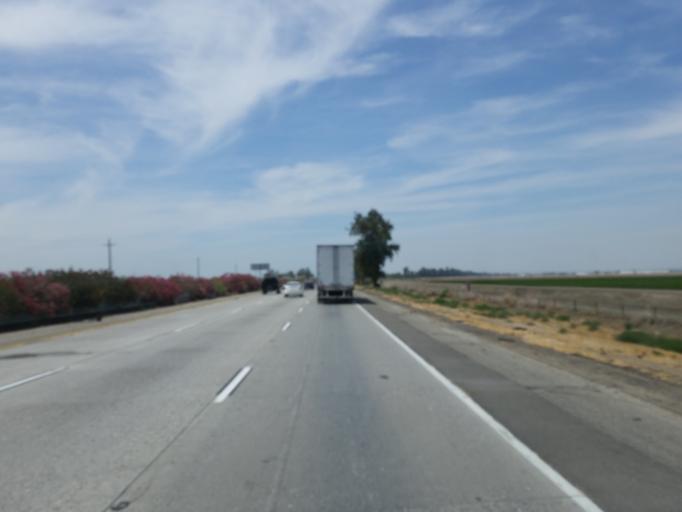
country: US
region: California
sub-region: Kern County
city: Greenfield
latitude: 35.1594
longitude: -118.9999
